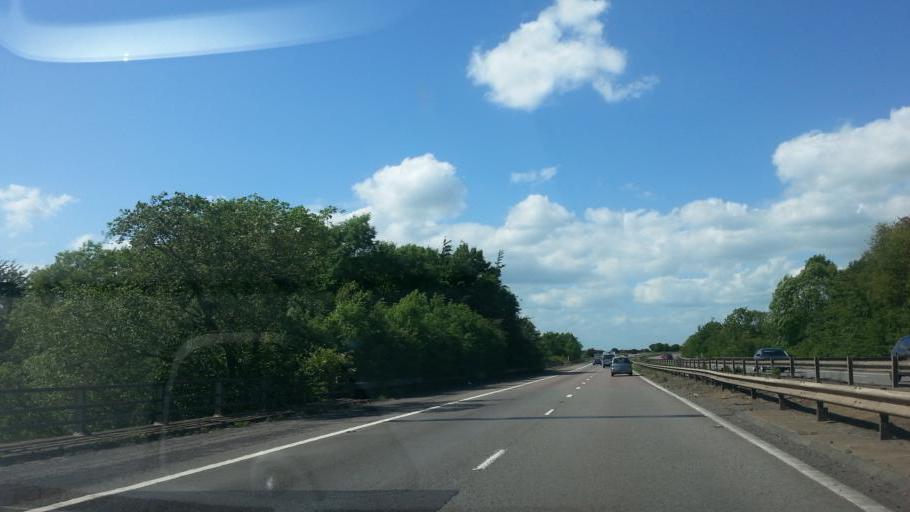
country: GB
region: England
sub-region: Central Bedfordshire
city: Stotfold
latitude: 52.0118
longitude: -0.2041
